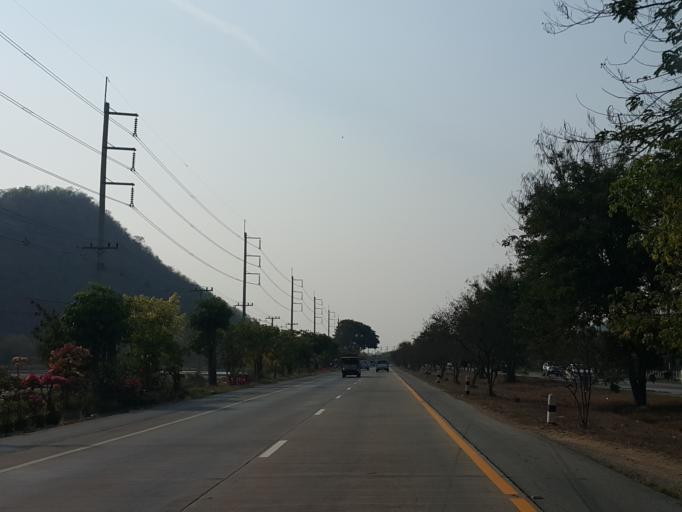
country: TH
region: Suphan Buri
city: Doembang Nangbuat
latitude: 14.8365
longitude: 100.1102
